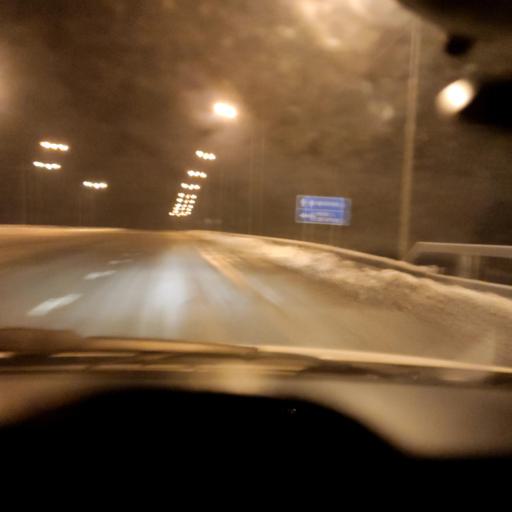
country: RU
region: Kursk
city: Fatezh
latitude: 52.0983
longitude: 35.8212
